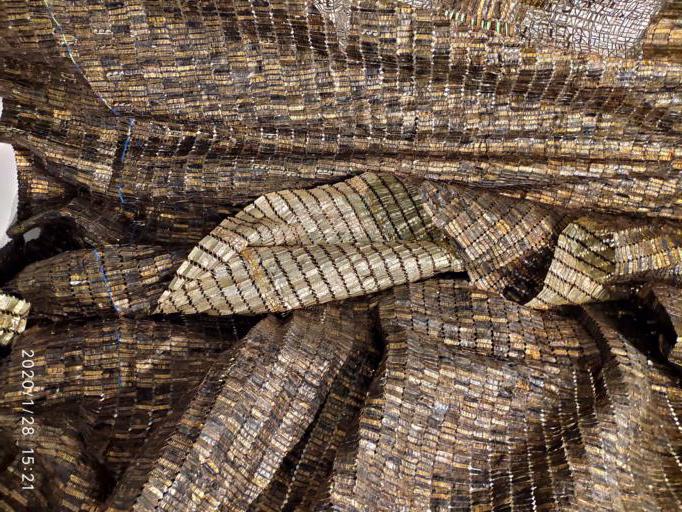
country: QA
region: Baladiyat ar Rayyan
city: Ar Rayyan
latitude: 25.3107
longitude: 51.4198
